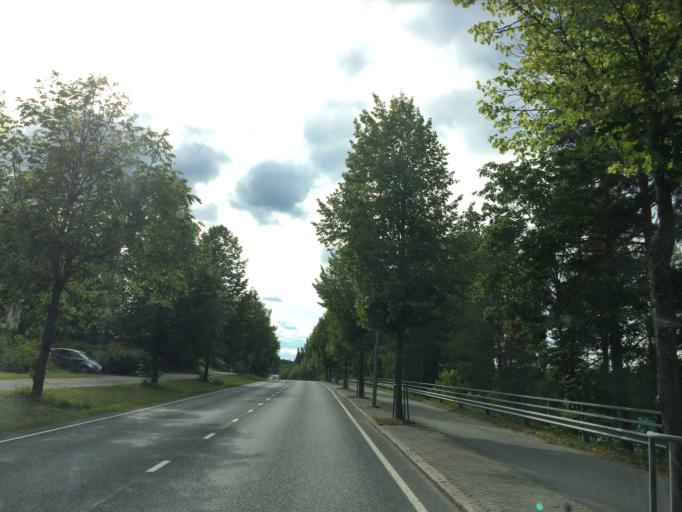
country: FI
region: Haeme
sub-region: Haemeenlinna
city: Turenki
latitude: 60.9201
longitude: 24.6271
